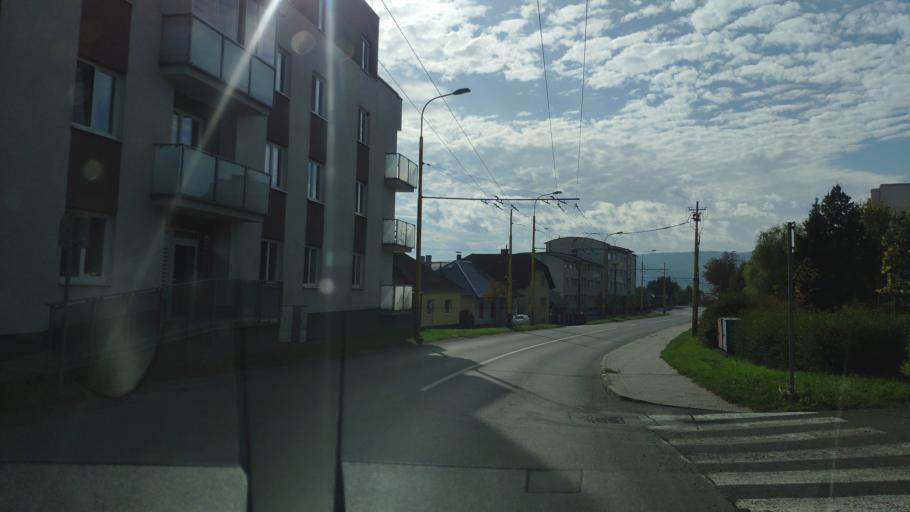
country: SK
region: Presovsky
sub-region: Okres Presov
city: Presov
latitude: 48.9777
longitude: 21.2687
